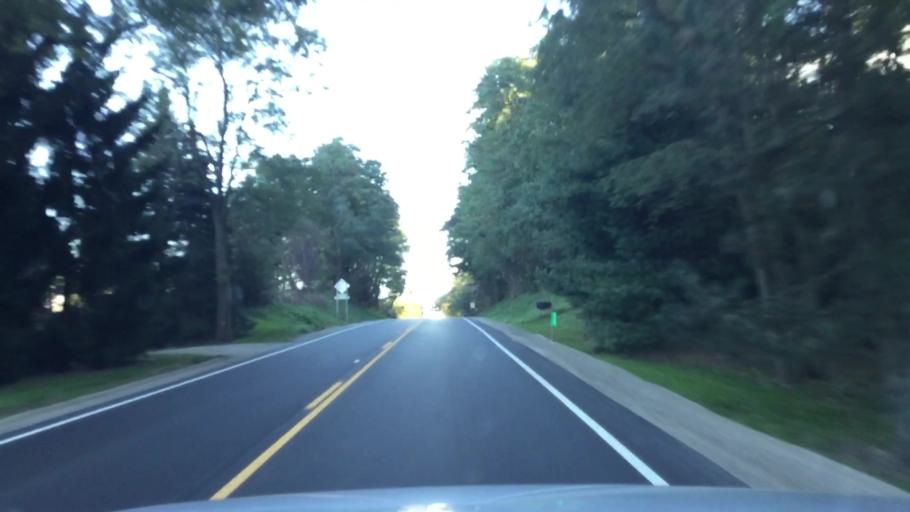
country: US
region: Michigan
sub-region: Lapeer County
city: Almont
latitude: 42.9156
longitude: -83.1434
